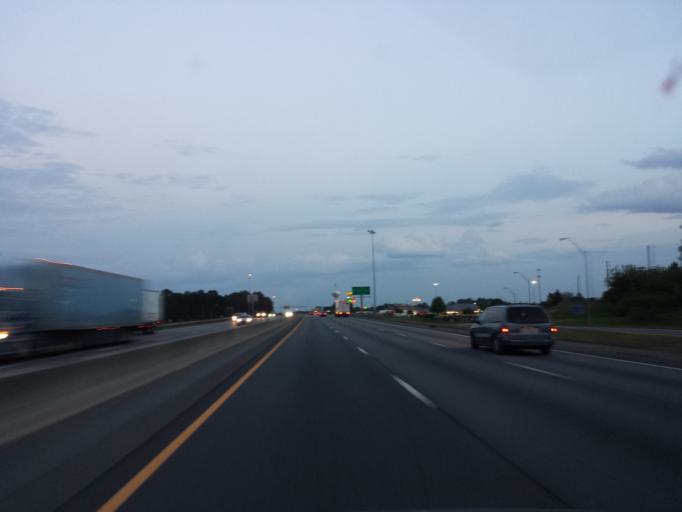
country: US
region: Georgia
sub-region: Tift County
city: Unionville
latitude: 31.4323
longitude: -83.5185
